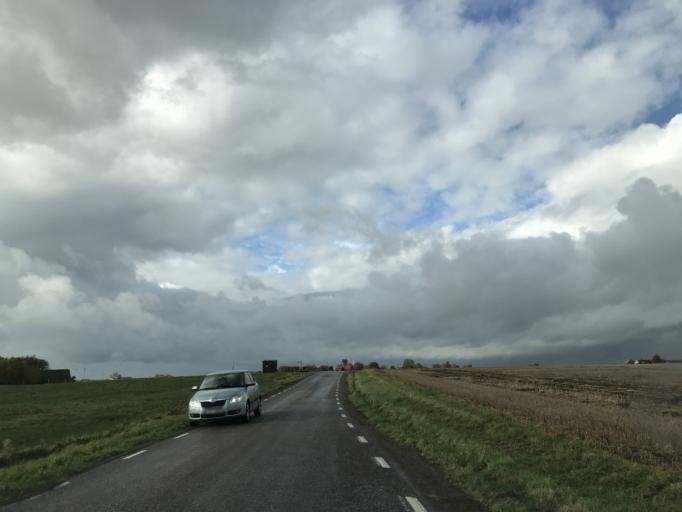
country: SE
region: Skane
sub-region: Svalovs Kommun
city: Svaloev
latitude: 55.9078
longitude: 13.1587
